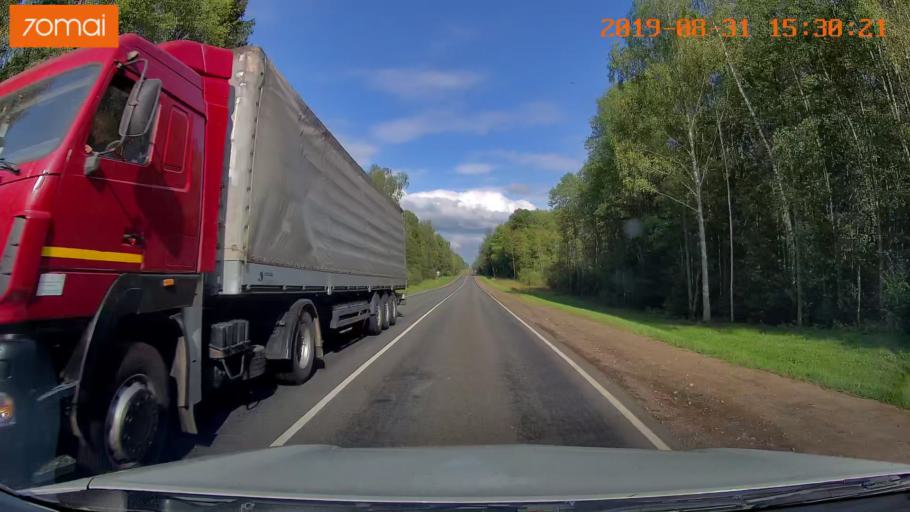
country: RU
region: Kaluga
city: Baryatino
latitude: 54.5751
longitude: 34.6279
